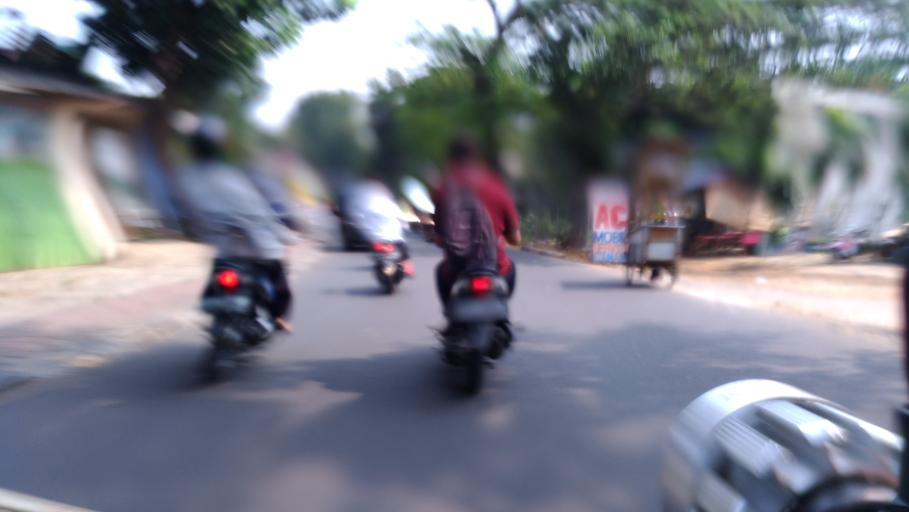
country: ID
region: West Java
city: Cileungsir
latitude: -6.3516
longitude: 106.8907
